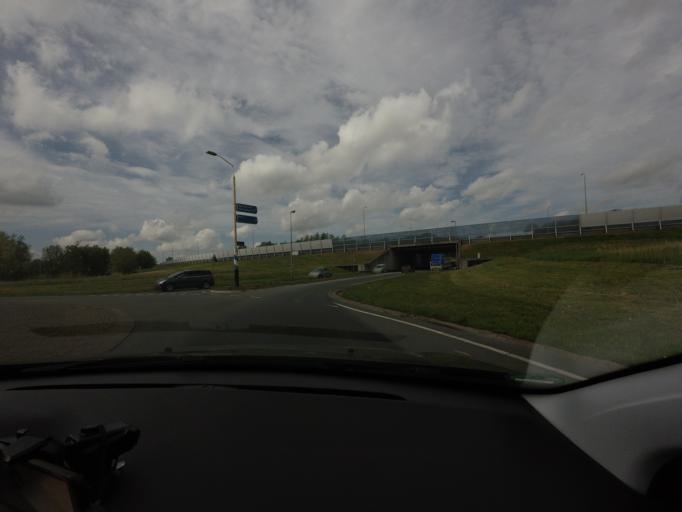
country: NL
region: North Holland
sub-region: Gemeente Beemster
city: Halfweg
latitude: 52.5042
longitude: 4.9349
